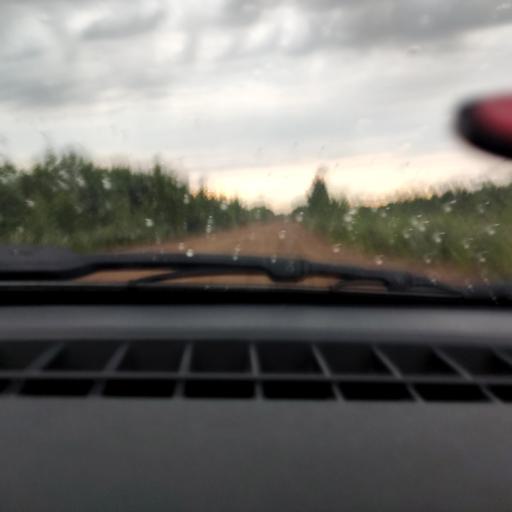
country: RU
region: Bashkortostan
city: Blagoveshchensk
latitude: 54.9209
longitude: 55.9738
